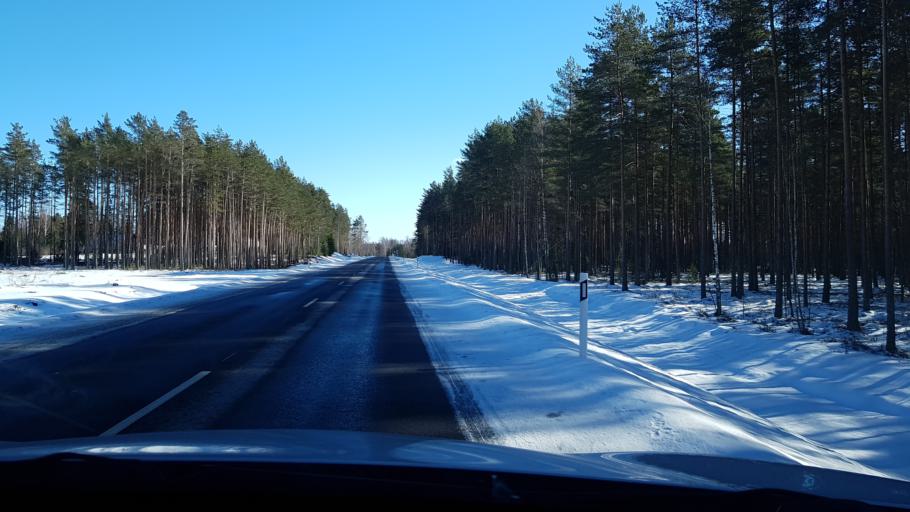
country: RU
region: Pskov
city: Pechory
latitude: 57.9617
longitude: 27.6110
